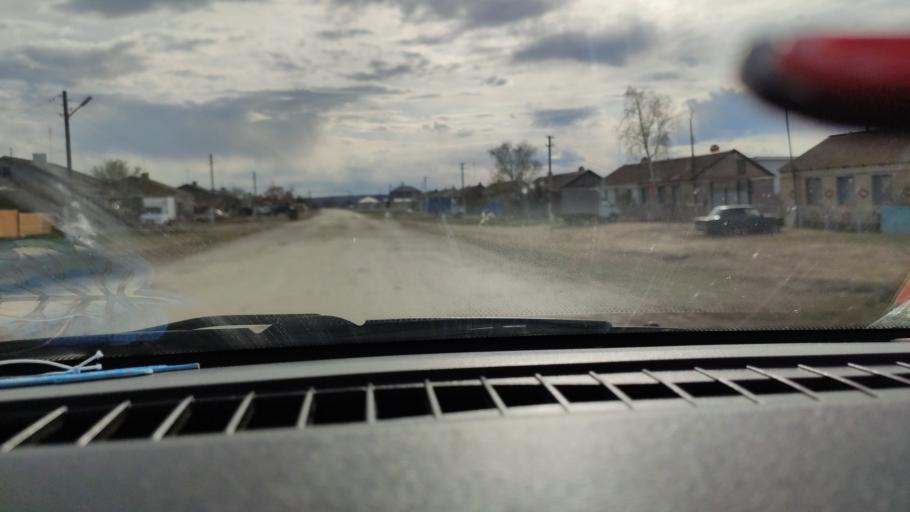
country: RU
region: Saratov
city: Rovnoye
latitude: 50.9307
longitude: 46.0879
